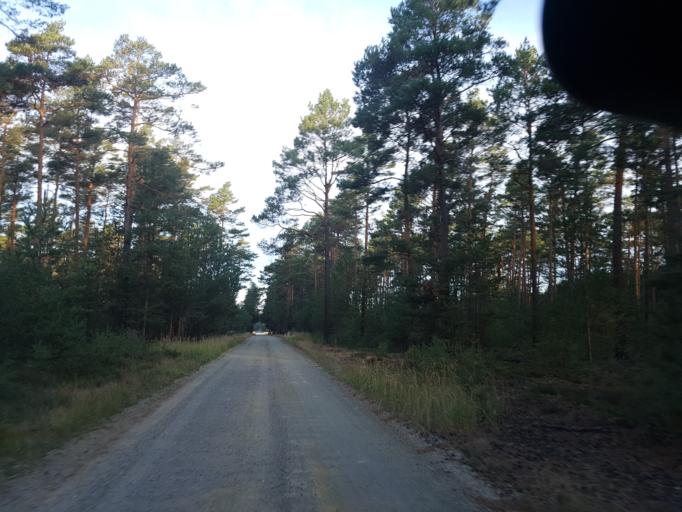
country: DE
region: Brandenburg
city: Schonewalde
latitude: 51.7420
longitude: 13.5720
